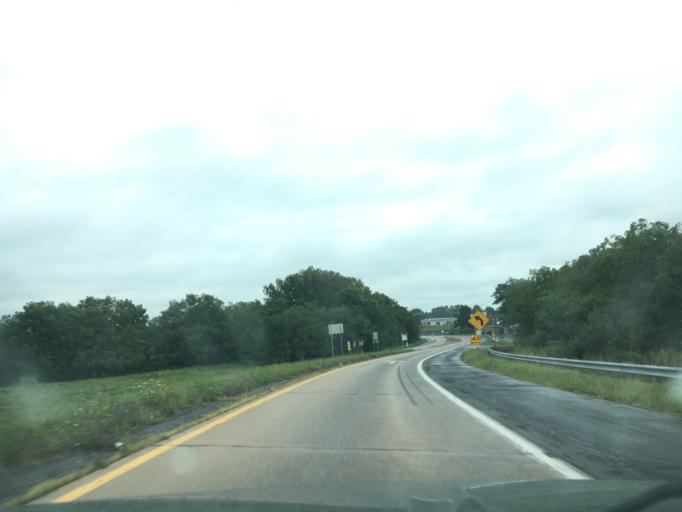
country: US
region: Pennsylvania
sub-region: Berks County
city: Kutztown
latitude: 40.4965
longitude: -75.8084
